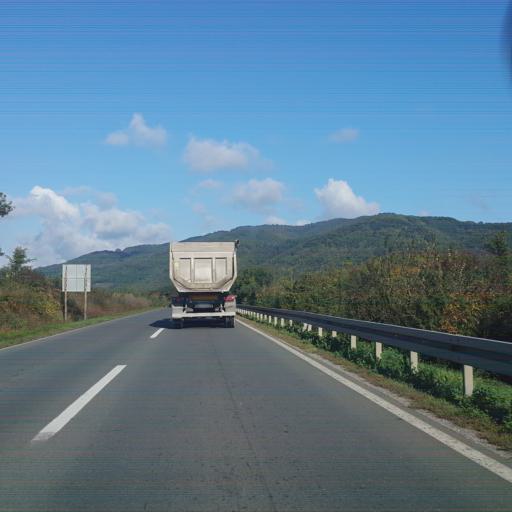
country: RS
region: Central Serbia
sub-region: Rasinski Okrug
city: Trstenik
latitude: 43.6266
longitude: 20.9736
